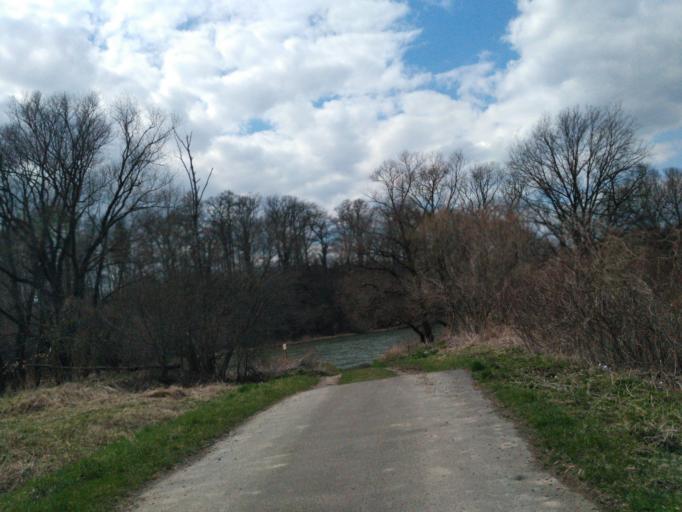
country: PL
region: Subcarpathian Voivodeship
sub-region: Powiat brzozowski
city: Dydnia
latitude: 49.6691
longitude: 22.2574
